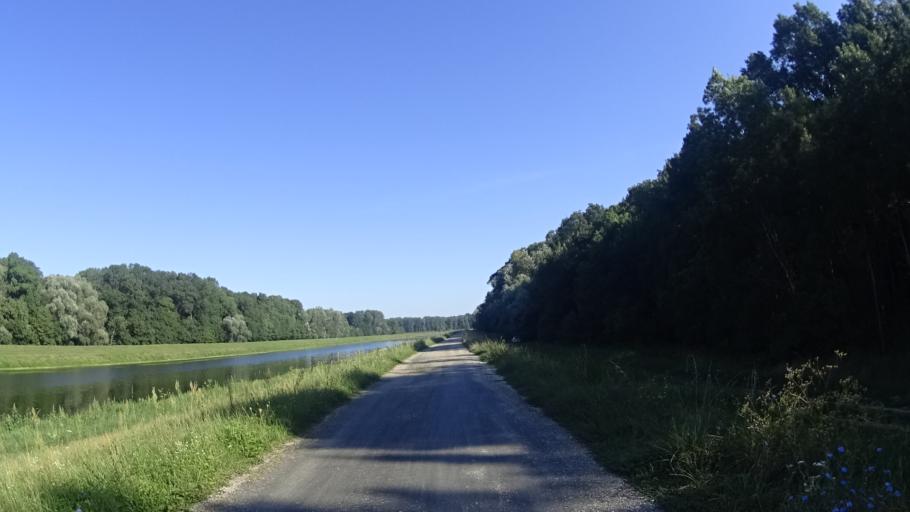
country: CZ
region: South Moravian
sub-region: Okres Breclav
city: Lanzhot
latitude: 48.6980
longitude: 16.9994
